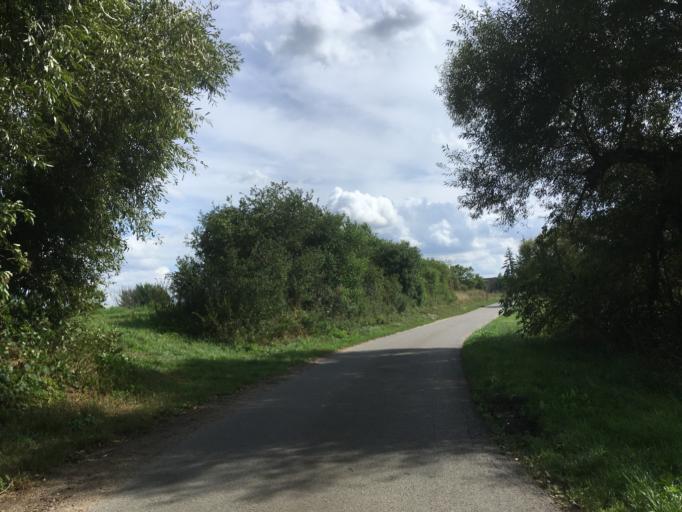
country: DE
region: Brandenburg
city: Gerswalde
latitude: 53.1265
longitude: 13.8458
